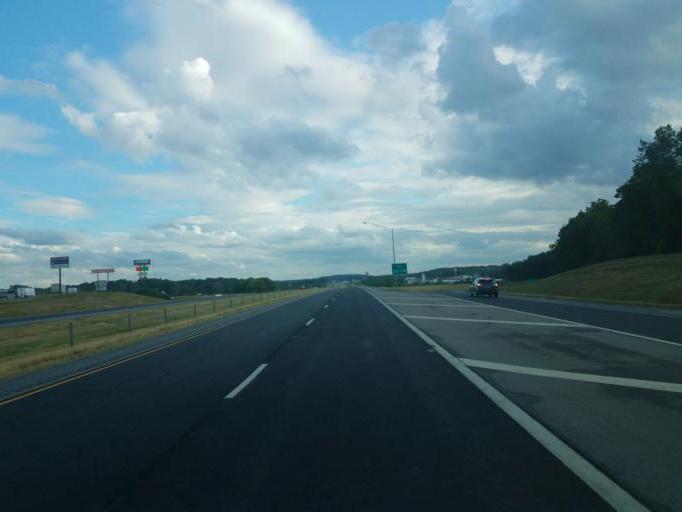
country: US
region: Indiana
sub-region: Steuben County
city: Fremont
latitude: 41.7521
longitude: -84.9938
